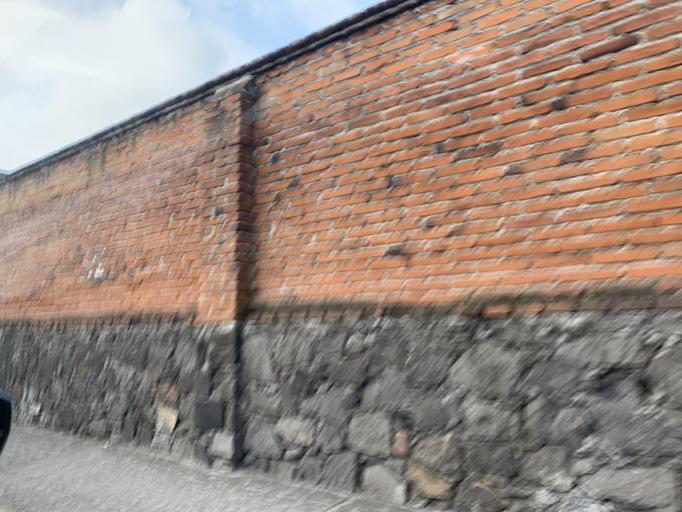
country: MX
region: Puebla
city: San Andres Cholula
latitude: 19.0503
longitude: -98.2984
